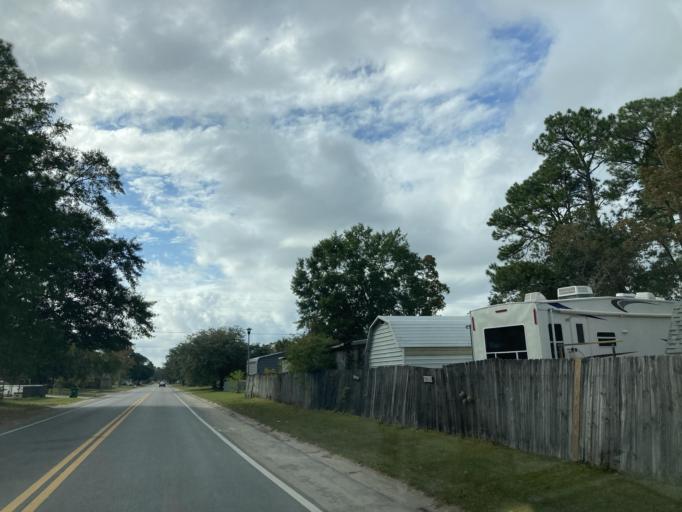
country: US
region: Mississippi
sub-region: Jackson County
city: Gulf Hills
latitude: 30.4360
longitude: -88.8214
